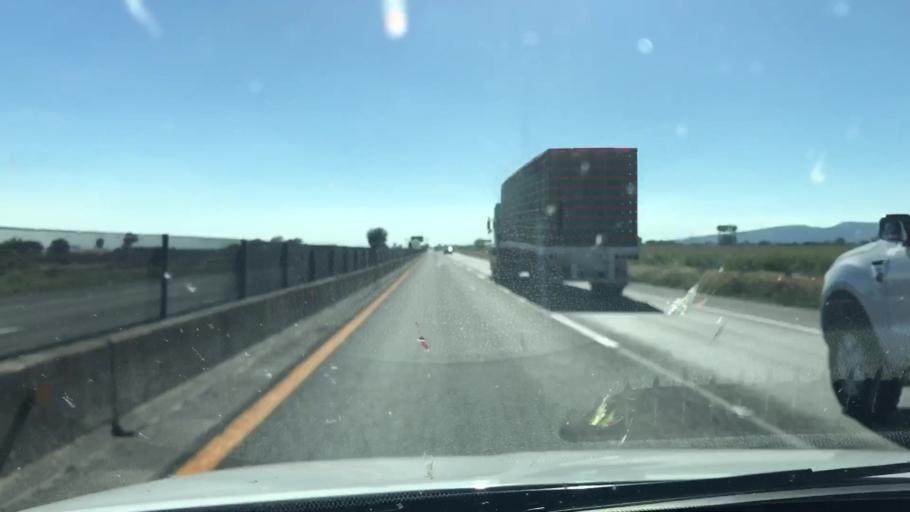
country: MX
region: Jalisco
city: Tepatitlan de Morelos
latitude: 20.8908
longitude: -102.7151
